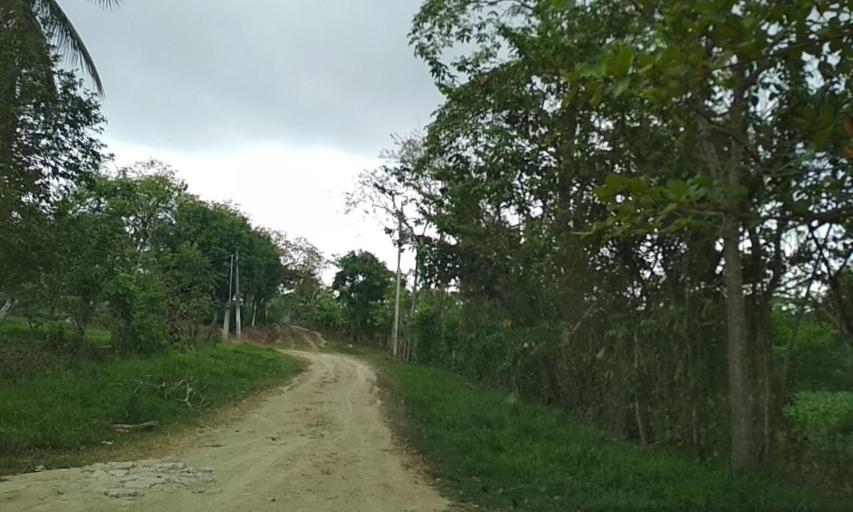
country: MX
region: Tabasco
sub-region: Huimanguillo
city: Francisco Rueda
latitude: 17.6566
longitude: -94.0971
